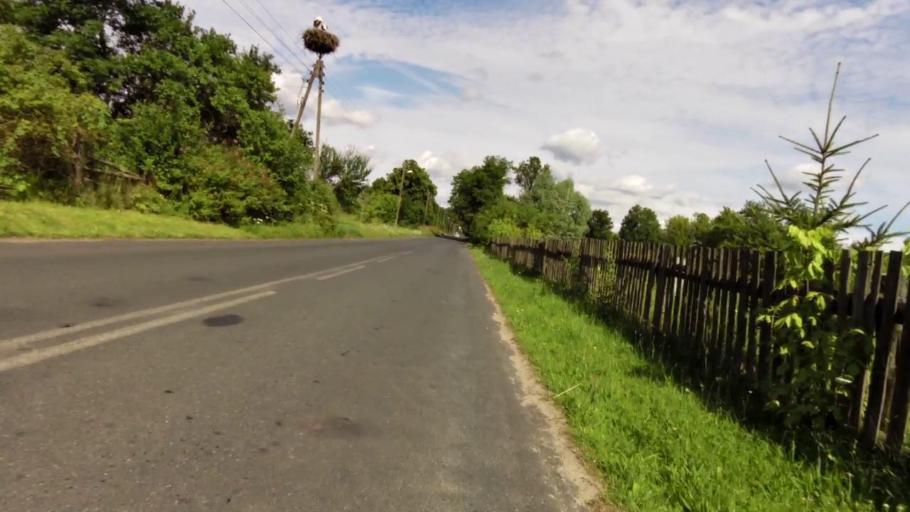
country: PL
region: West Pomeranian Voivodeship
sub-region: Powiat stargardzki
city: Dobrzany
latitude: 53.4061
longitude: 15.4310
